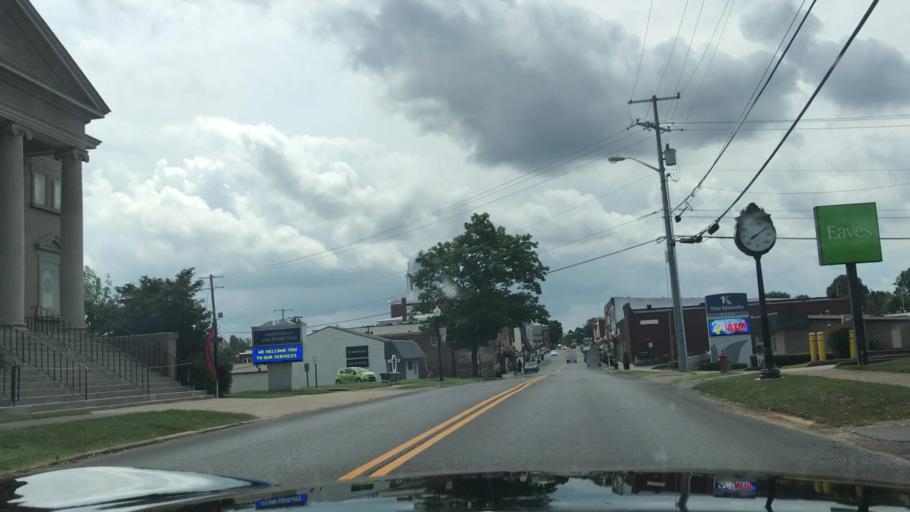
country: US
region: Kentucky
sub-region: Muhlenberg County
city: Greenville
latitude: 37.2032
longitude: -87.1789
